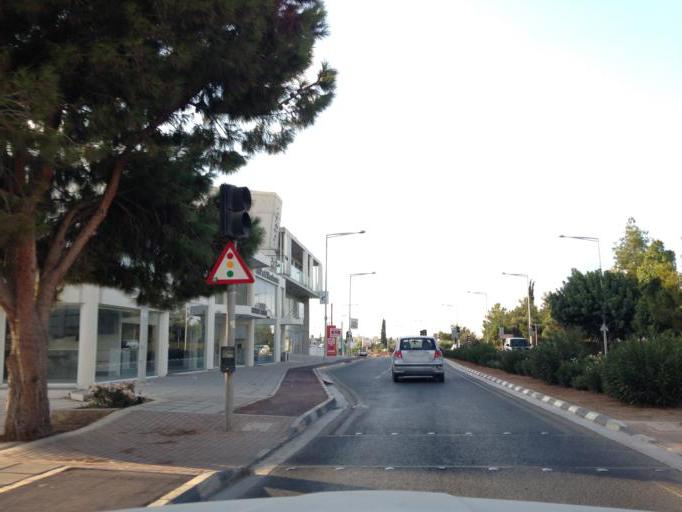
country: CY
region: Pafos
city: Paphos
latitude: 34.7656
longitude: 32.4458
